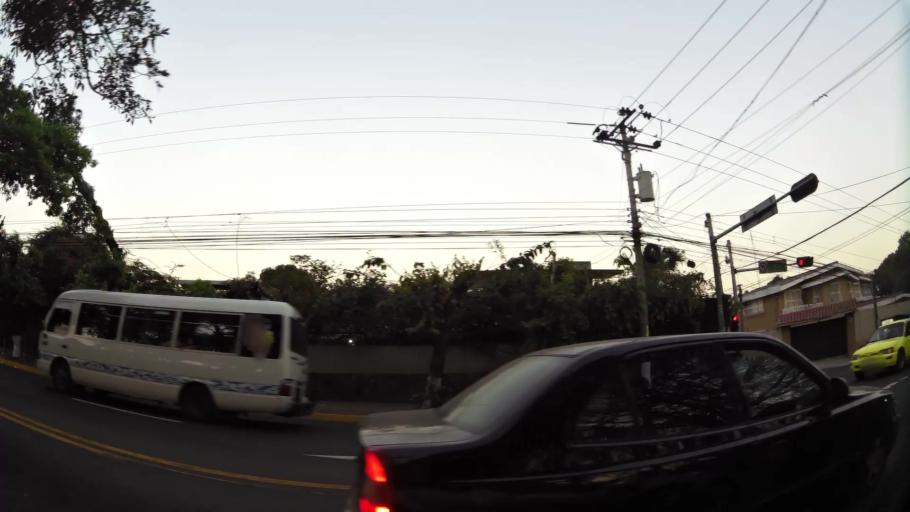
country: SV
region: San Salvador
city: Mejicanos
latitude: 13.7043
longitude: -89.2260
